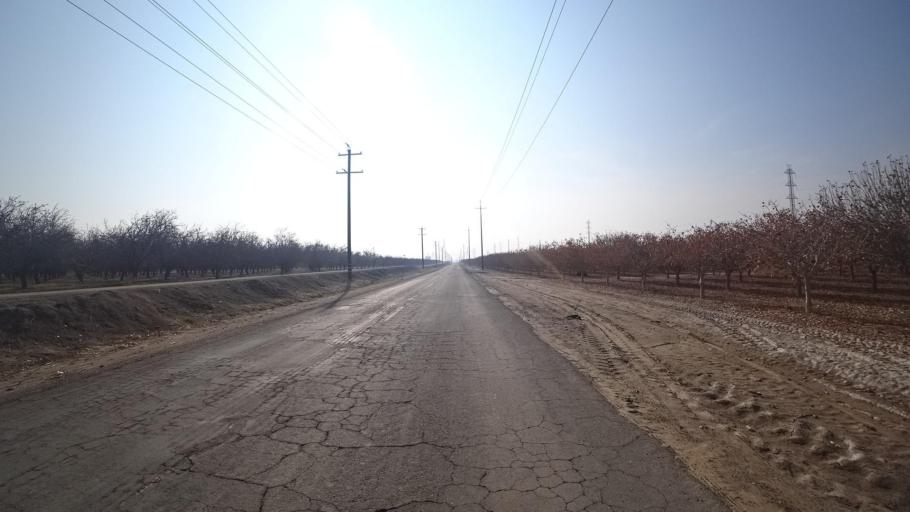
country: US
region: California
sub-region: Kern County
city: Buttonwillow
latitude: 35.4106
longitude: -119.4475
